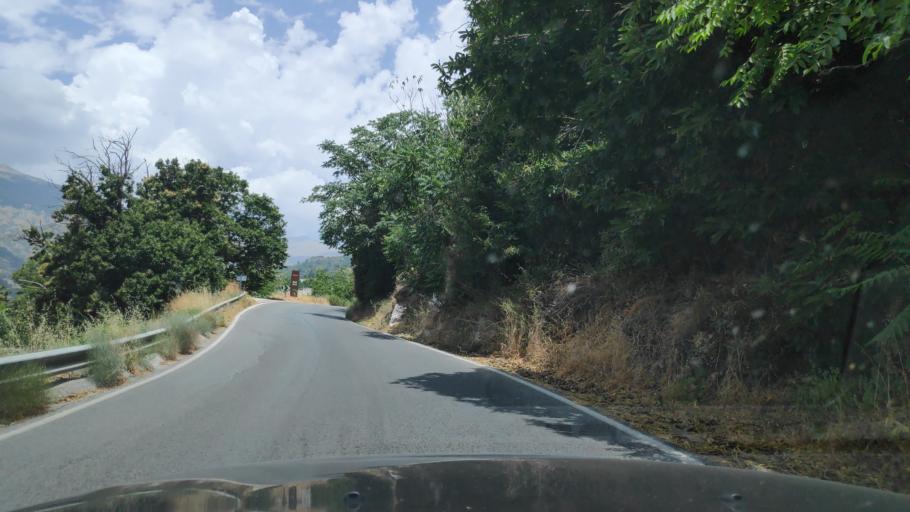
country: ES
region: Andalusia
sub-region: Provincia de Granada
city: Bubion
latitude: 36.9438
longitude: -3.3546
